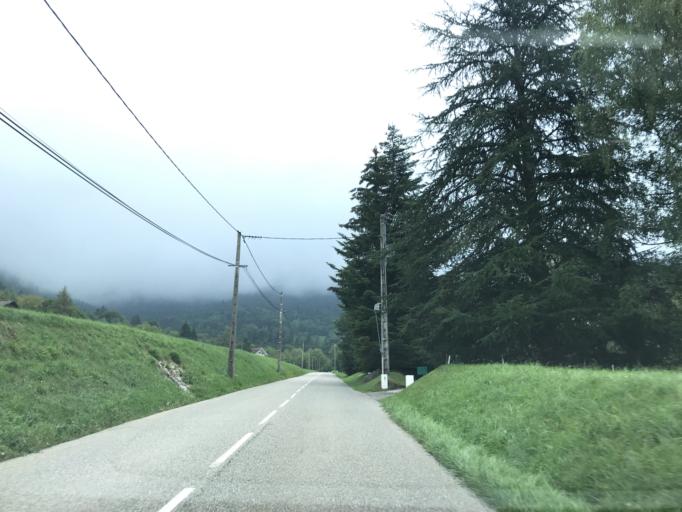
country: FR
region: Rhone-Alpes
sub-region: Departement de la Haute-Savoie
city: Talloires
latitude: 45.8345
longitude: 6.2341
